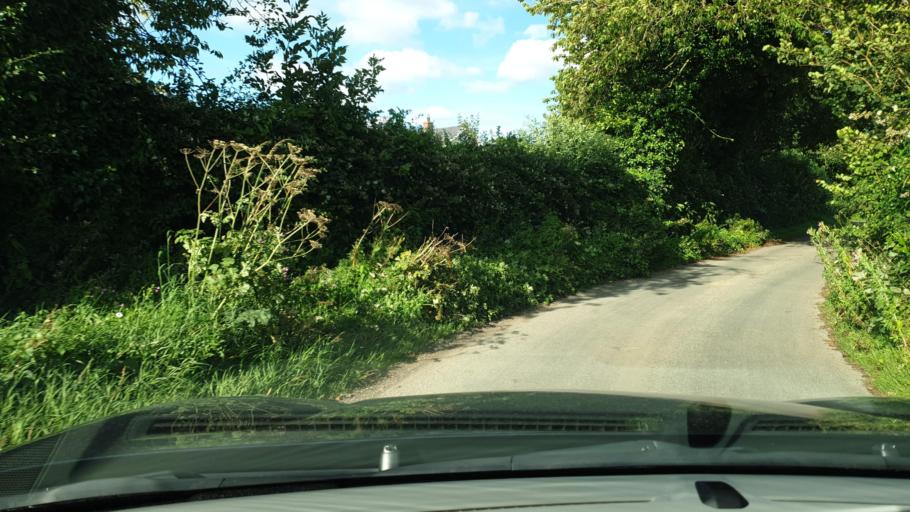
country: IE
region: Leinster
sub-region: An Mhi
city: Ashbourne
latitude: 53.5865
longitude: -6.3503
